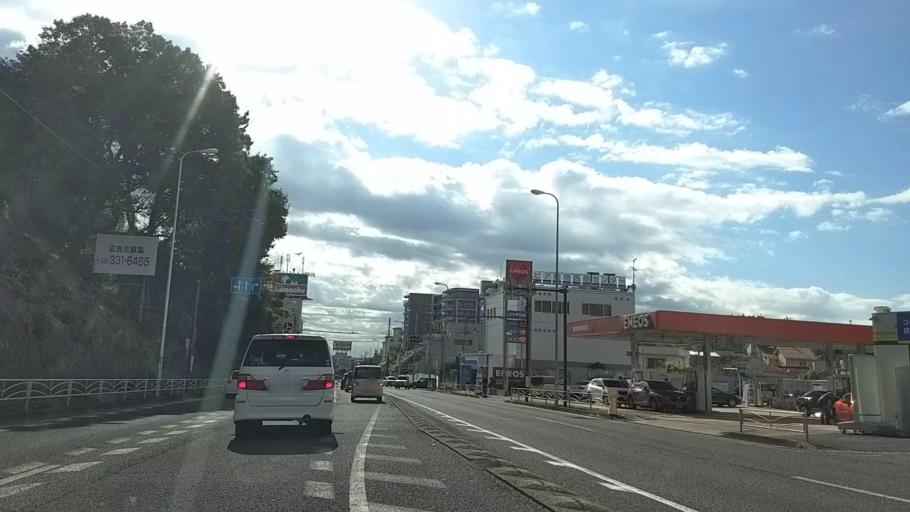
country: JP
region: Kanagawa
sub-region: Kawasaki-shi
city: Kawasaki
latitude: 35.5032
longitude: 139.6621
